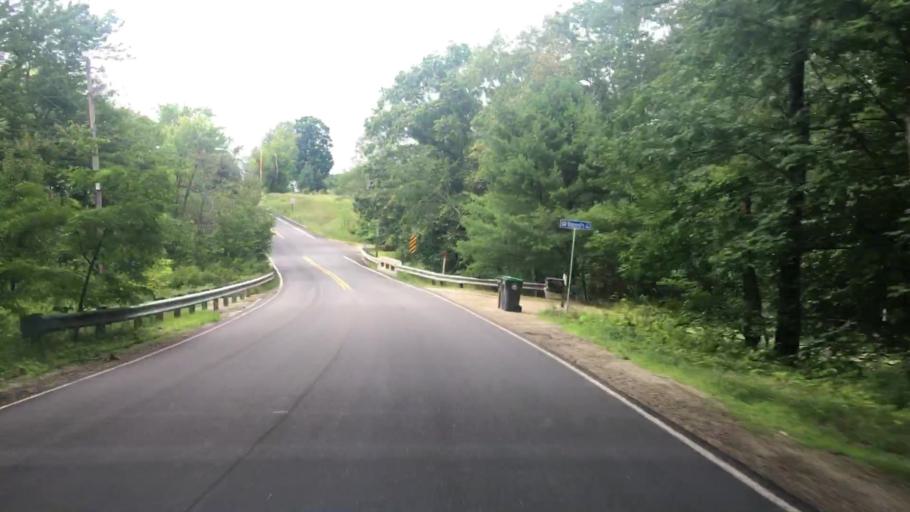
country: US
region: Maine
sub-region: York County
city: West Kennebunk
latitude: 43.4571
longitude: -70.6054
